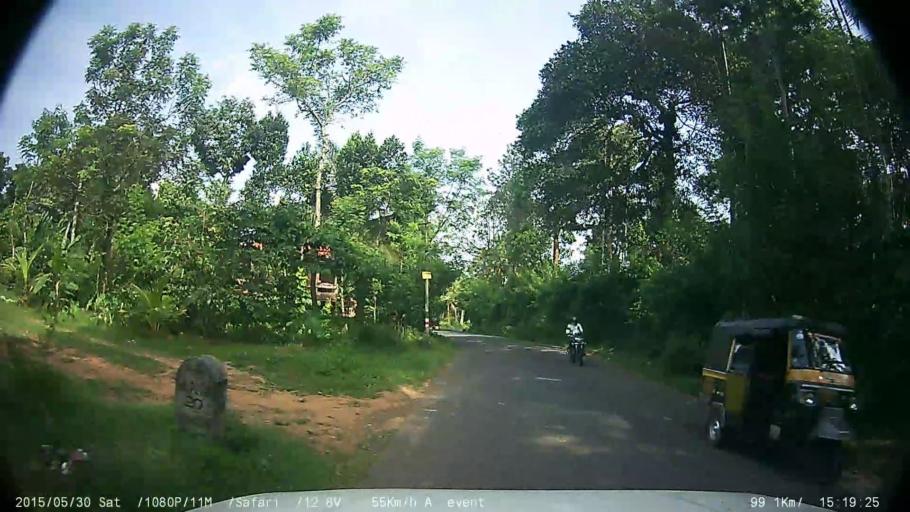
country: IN
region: Kerala
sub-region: Wayanad
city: Panamaram
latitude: 11.7589
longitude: 76.0638
